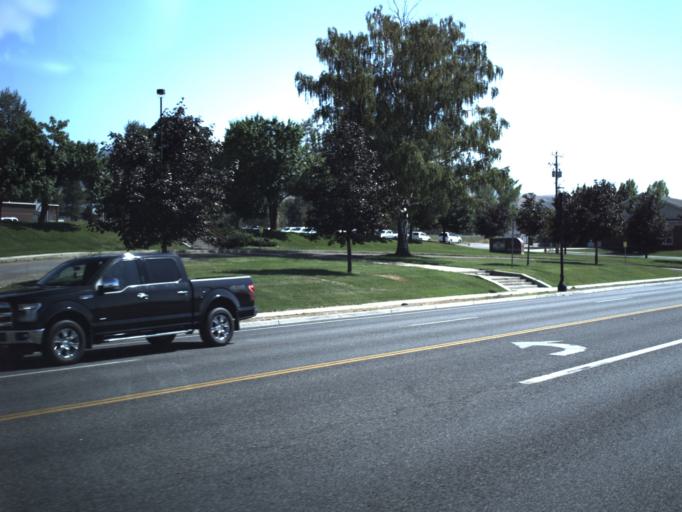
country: US
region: Utah
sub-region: Cache County
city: Richmond
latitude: 41.9116
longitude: -111.8147
